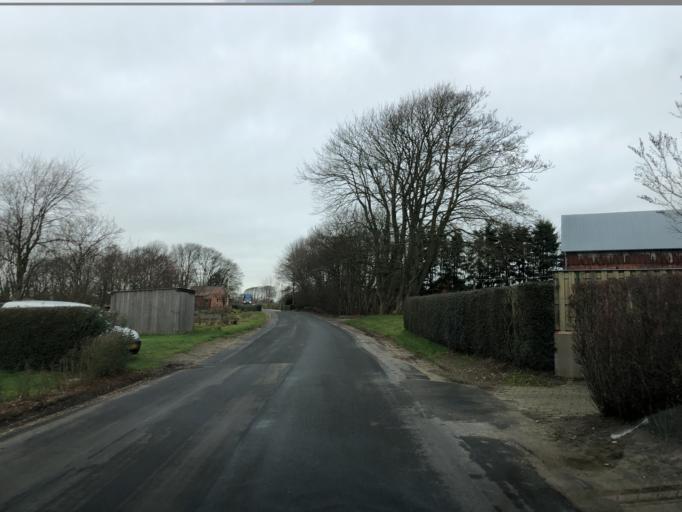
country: DK
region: Central Jutland
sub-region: Viborg Kommune
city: Stoholm
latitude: 56.4474
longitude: 9.1084
